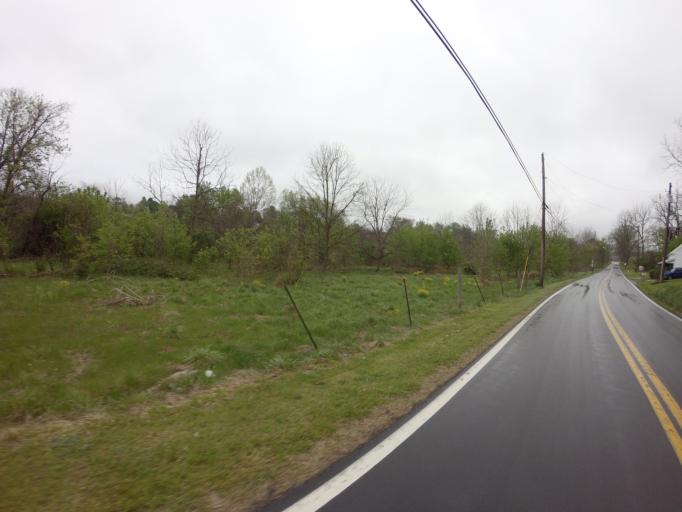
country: US
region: Maryland
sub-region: Frederick County
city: Myersville
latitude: 39.4876
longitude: -77.5343
